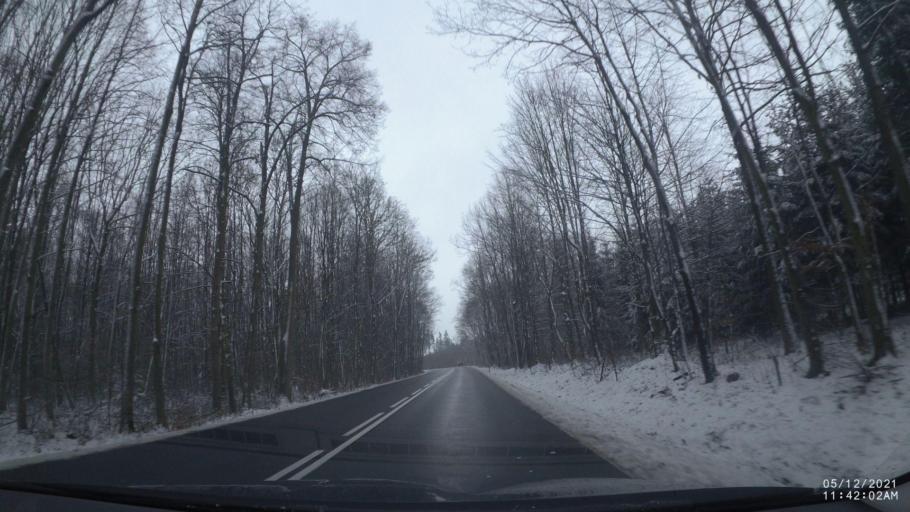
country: CZ
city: Dobruska
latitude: 50.2742
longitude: 16.1927
